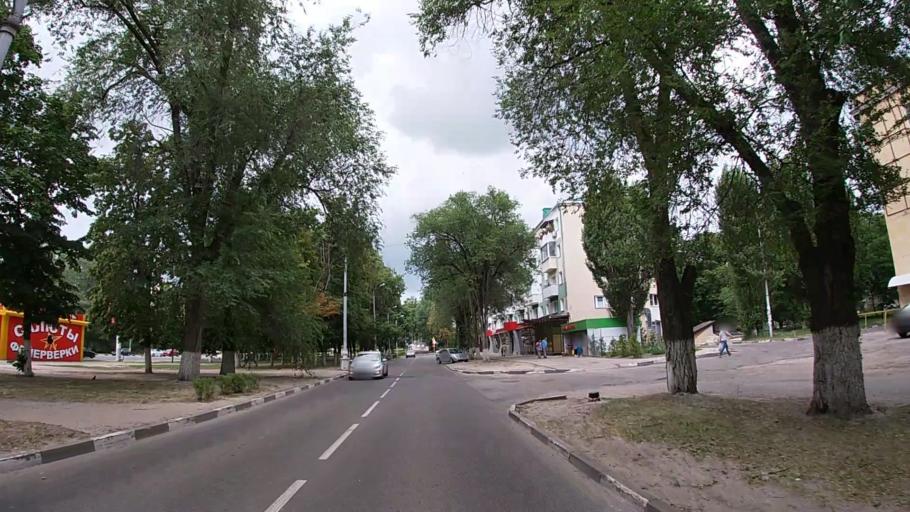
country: RU
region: Belgorod
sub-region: Belgorodskiy Rayon
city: Belgorod
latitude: 50.6134
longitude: 36.5790
